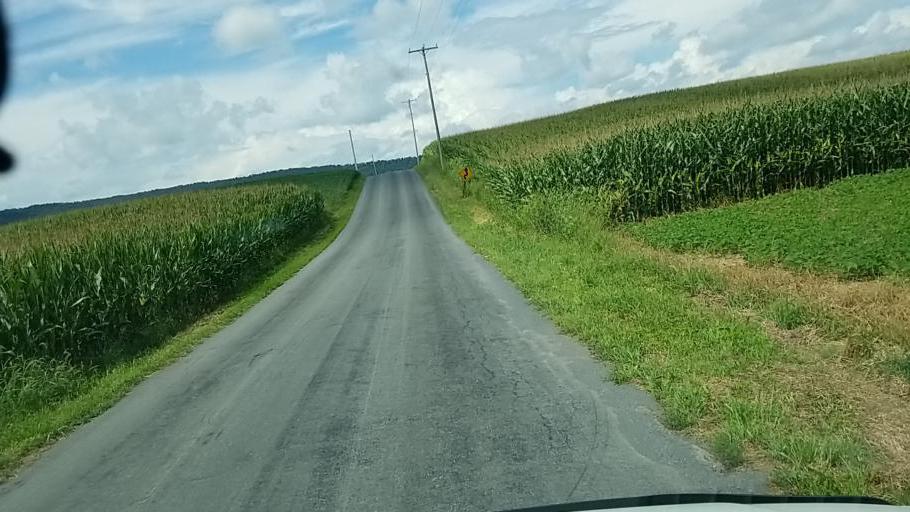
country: US
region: Pennsylvania
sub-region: Dauphin County
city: Elizabethville
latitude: 40.5941
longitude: -76.8467
